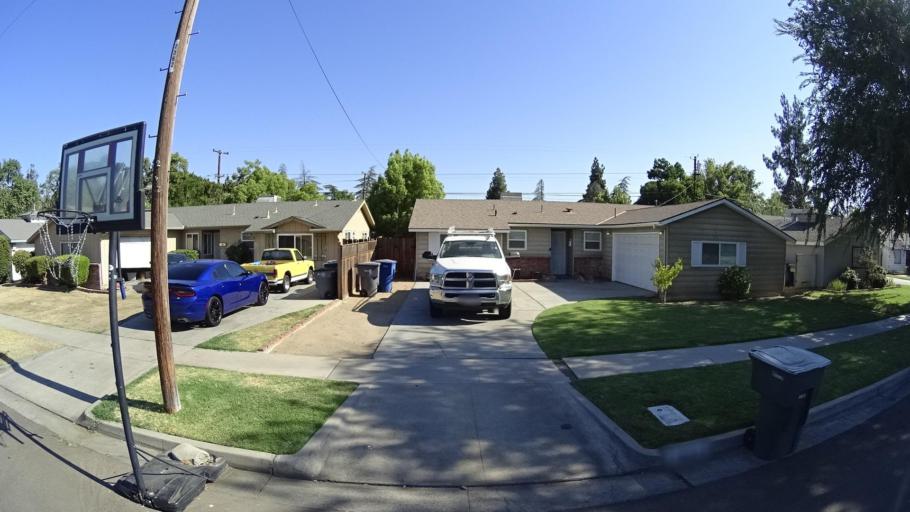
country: US
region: California
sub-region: Fresno County
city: Fresno
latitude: 36.7930
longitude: -119.7579
